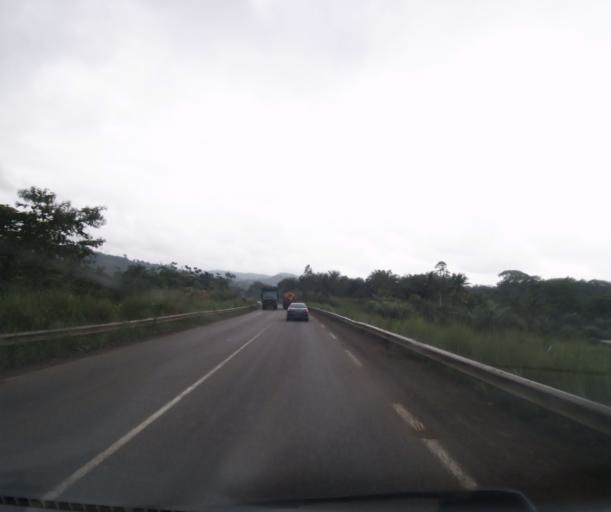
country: CM
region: Littoral
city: Edea
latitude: 3.7891
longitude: 10.2058
